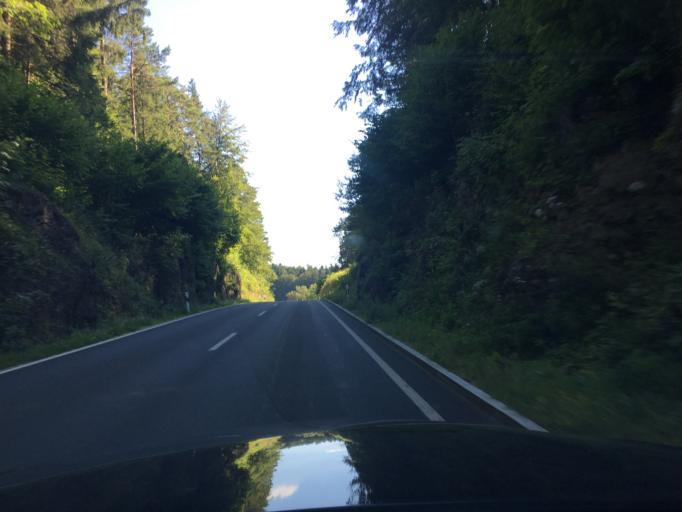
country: DE
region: Bavaria
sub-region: Upper Franconia
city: Obertrubach
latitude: 49.6777
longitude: 11.3604
